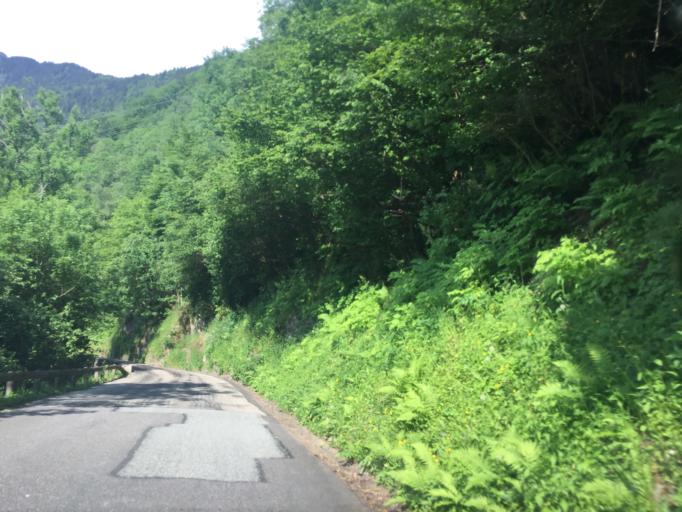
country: FR
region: Rhone-Alpes
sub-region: Departement de la Savoie
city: Aiton
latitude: 45.5242
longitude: 6.3267
